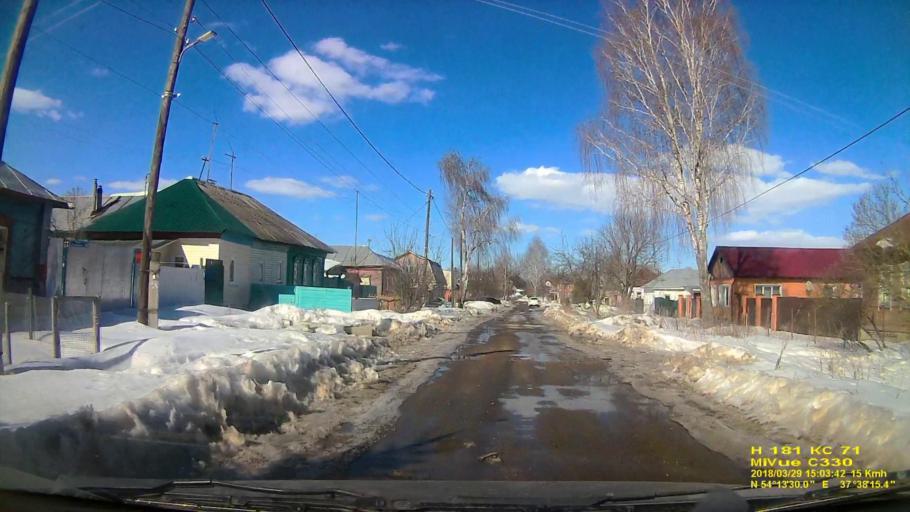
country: RU
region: Tula
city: Tula
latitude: 54.2250
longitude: 37.6376
